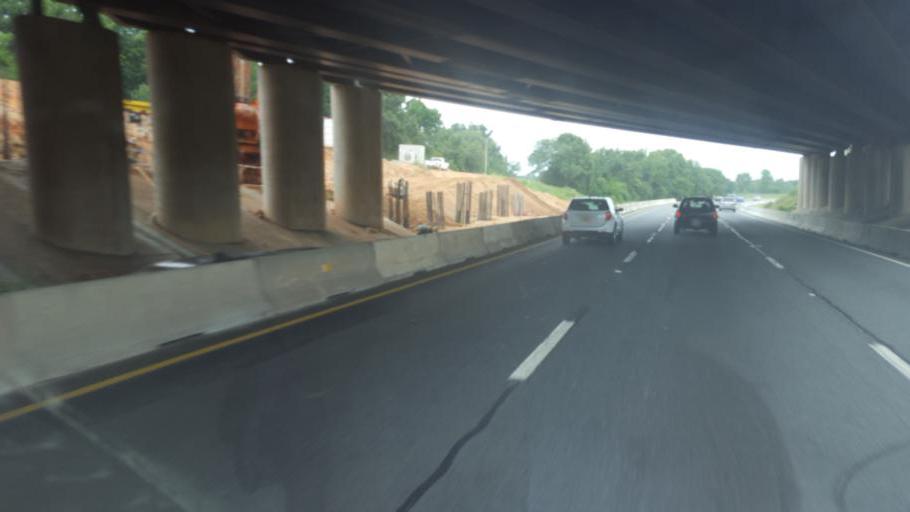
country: US
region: North Carolina
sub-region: Mecklenburg County
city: Charlotte
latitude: 35.2683
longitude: -80.8452
